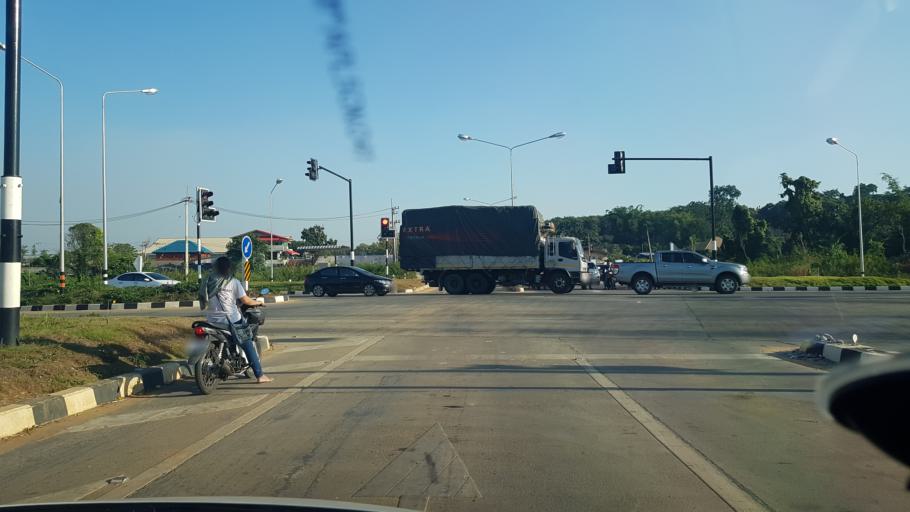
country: TH
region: Chiang Rai
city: Chiang Rai
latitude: 19.9404
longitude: 99.8071
